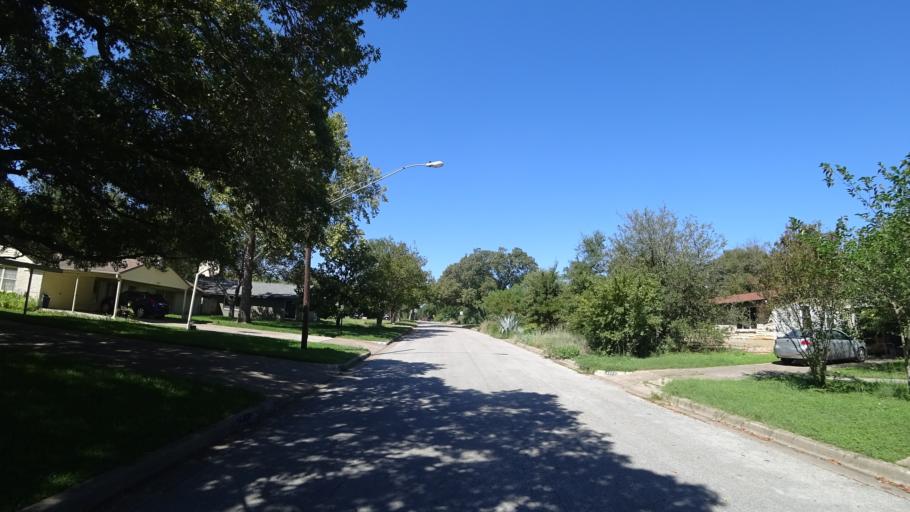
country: US
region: Texas
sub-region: Travis County
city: Austin
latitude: 30.3124
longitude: -97.6982
